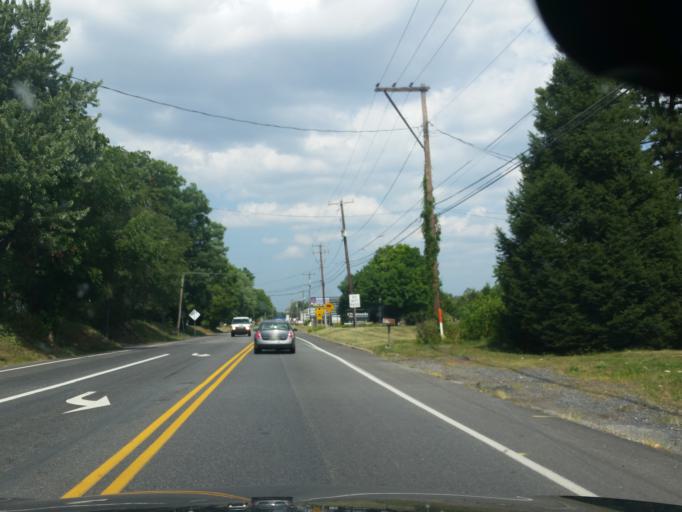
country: US
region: Pennsylvania
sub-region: Cumberland County
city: Mechanicsburg
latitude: 40.2213
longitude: -76.9819
